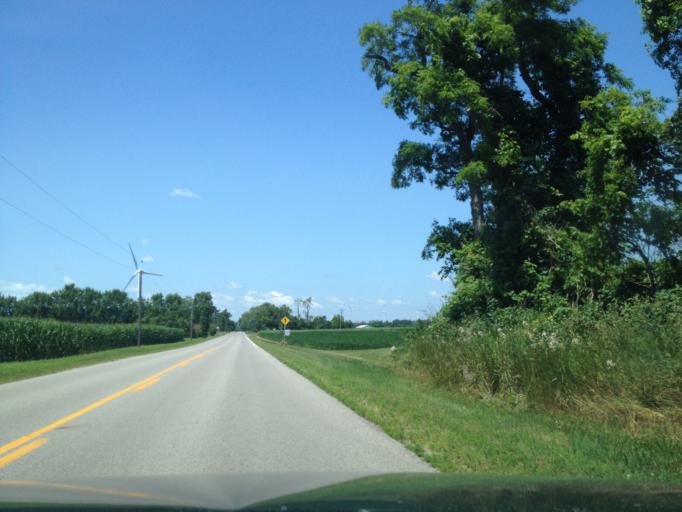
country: CA
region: Ontario
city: Aylmer
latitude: 42.6110
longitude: -80.6888
